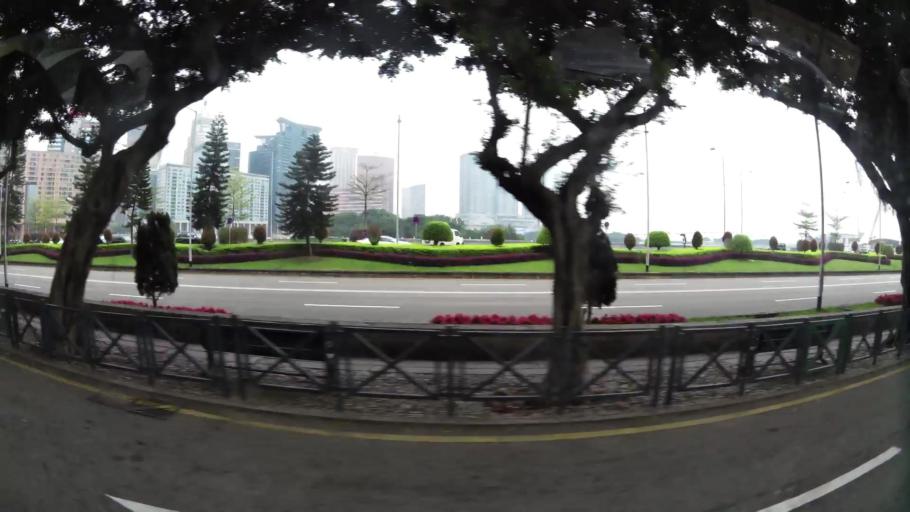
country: MO
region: Macau
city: Macau
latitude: 22.1878
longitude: 113.5376
